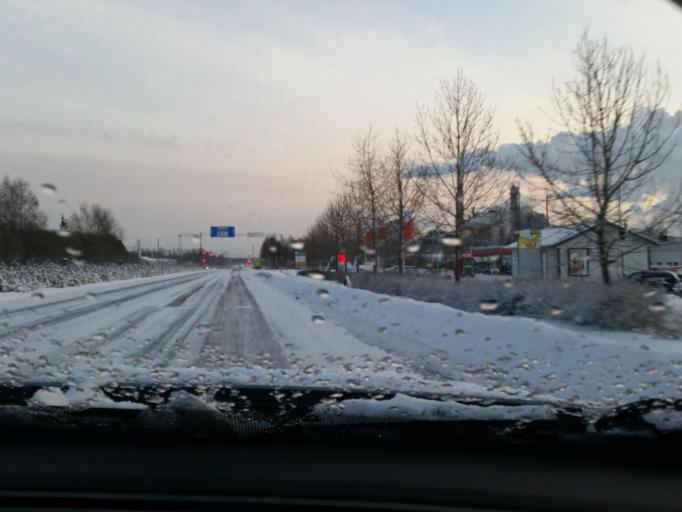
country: SE
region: Norrbotten
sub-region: Pitea Kommun
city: Pitea
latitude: 65.3197
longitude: 21.4317
